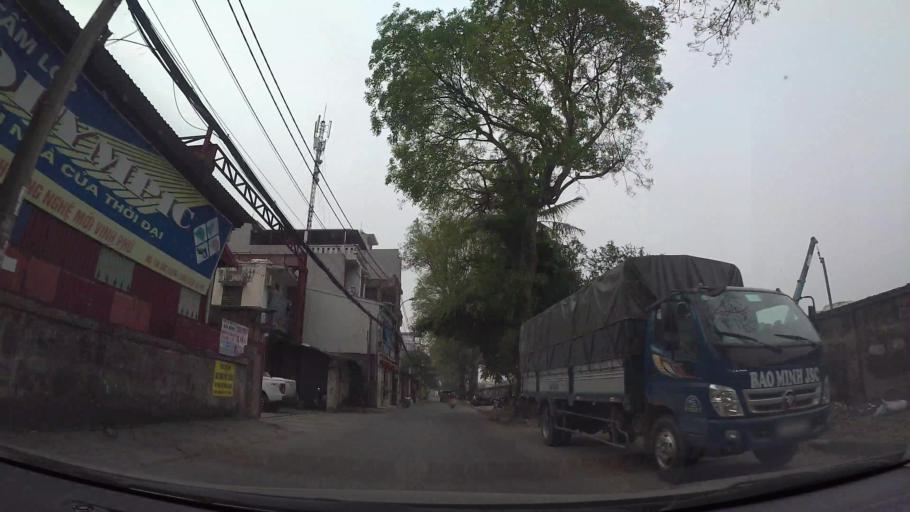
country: VN
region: Ha Noi
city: Hoan Kiem
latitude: 21.0676
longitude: 105.8853
